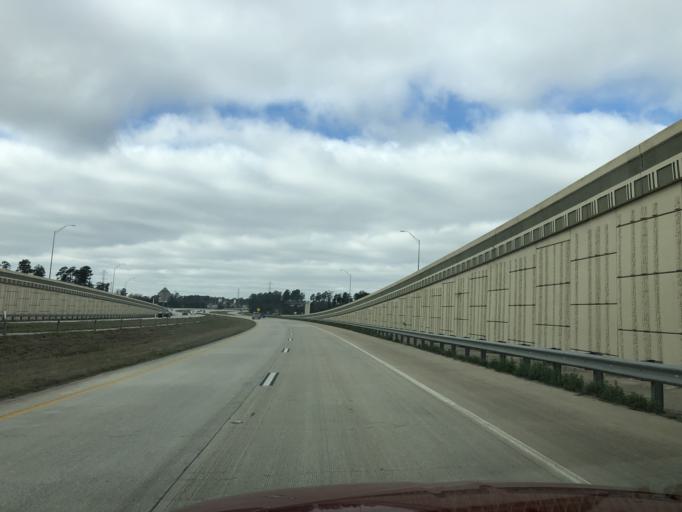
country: US
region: Texas
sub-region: Harris County
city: Spring
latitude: 30.0922
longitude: -95.4401
